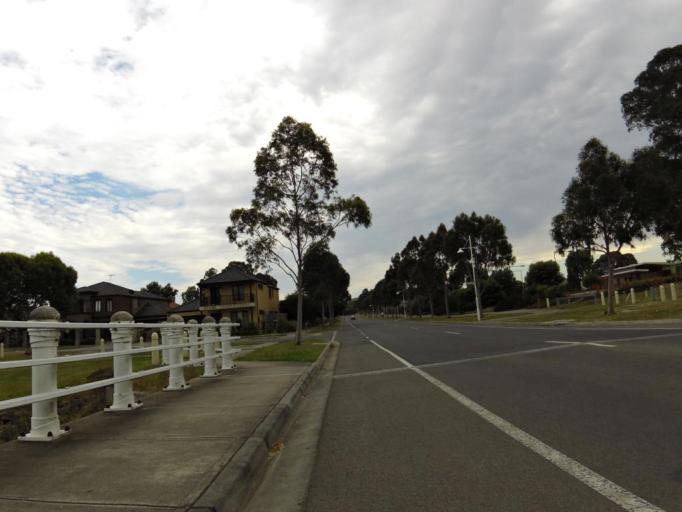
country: AU
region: Victoria
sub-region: Whittlesea
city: Mill Park
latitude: -37.6402
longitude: 145.0762
